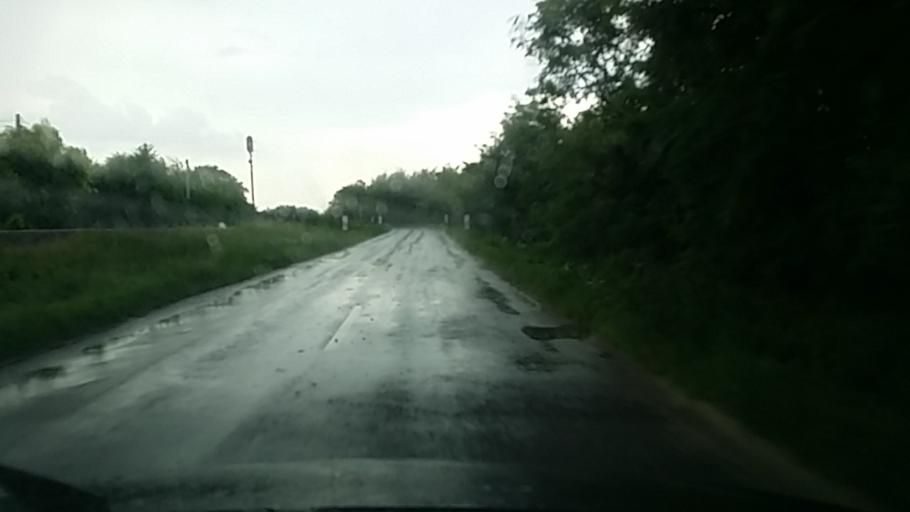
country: HU
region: Pest
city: Ocsa
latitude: 47.2907
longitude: 19.2564
